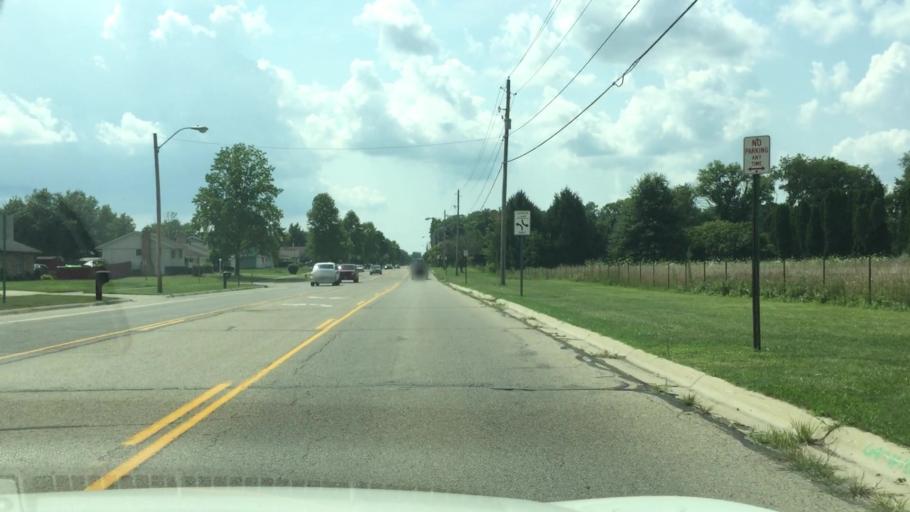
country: US
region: Ohio
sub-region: Clark County
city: Northridge
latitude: 39.9658
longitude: -83.7688
